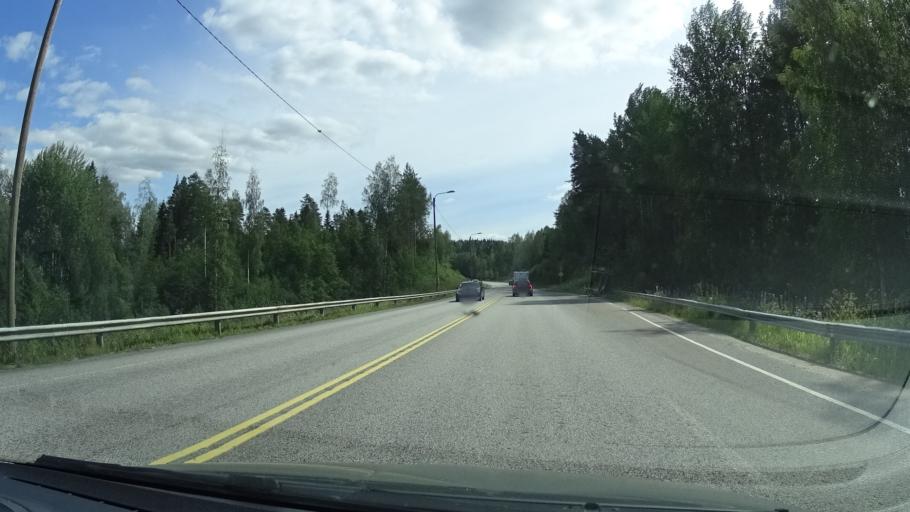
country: FI
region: Central Finland
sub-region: Jyvaeskylae
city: Jyvaeskylae
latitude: 62.2669
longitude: 25.5579
